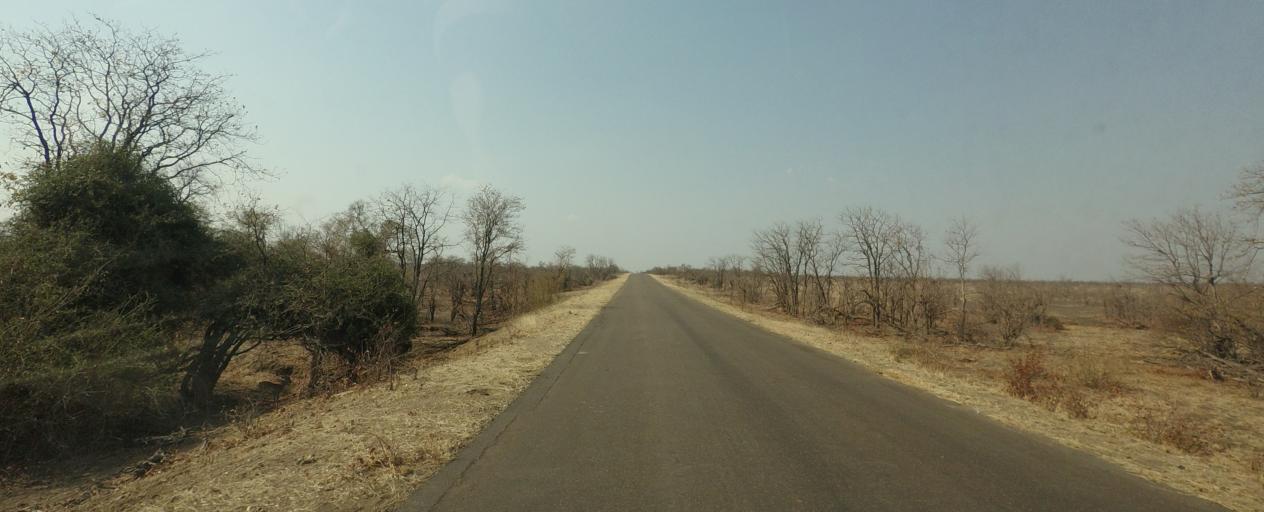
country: ZA
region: Limpopo
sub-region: Mopani District Municipality
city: Giyani
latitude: -23.1298
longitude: 31.3800
